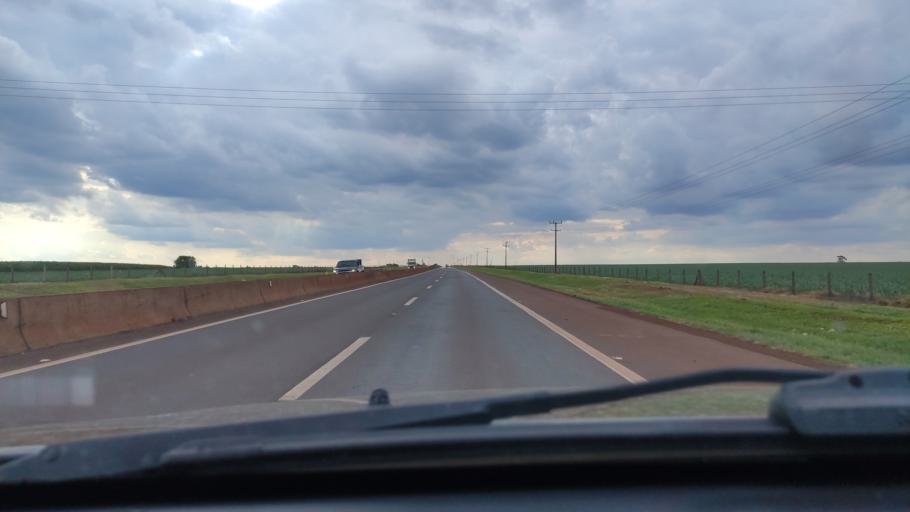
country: BR
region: Sao Paulo
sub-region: Palmital
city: Palmital
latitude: -22.8228
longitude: -50.0397
